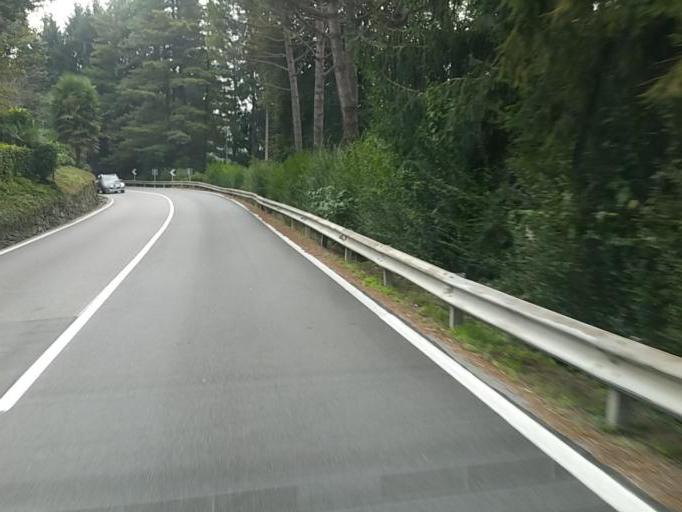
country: IT
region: Piedmont
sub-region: Provincia di Novara
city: Bolzano Novarese
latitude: 45.7680
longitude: 8.4290
